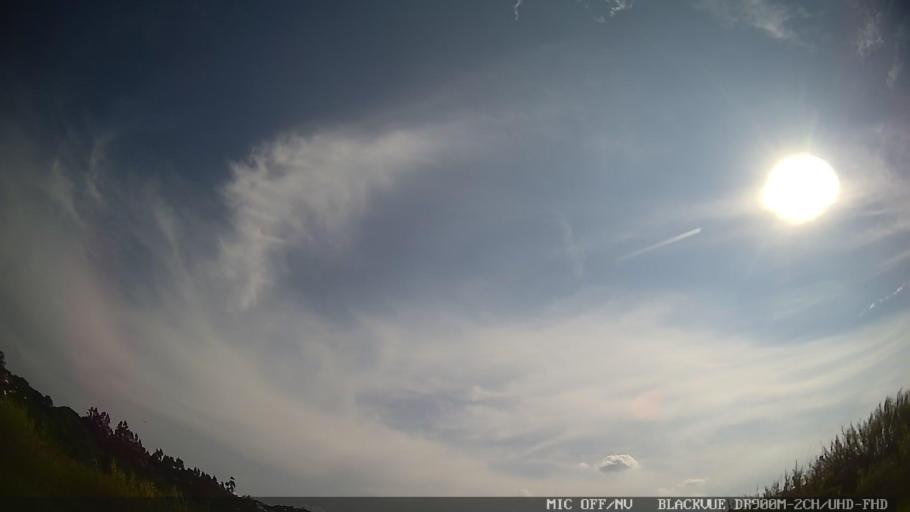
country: BR
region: Sao Paulo
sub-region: Braganca Paulista
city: Braganca Paulista
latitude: -22.9509
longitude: -46.5521
